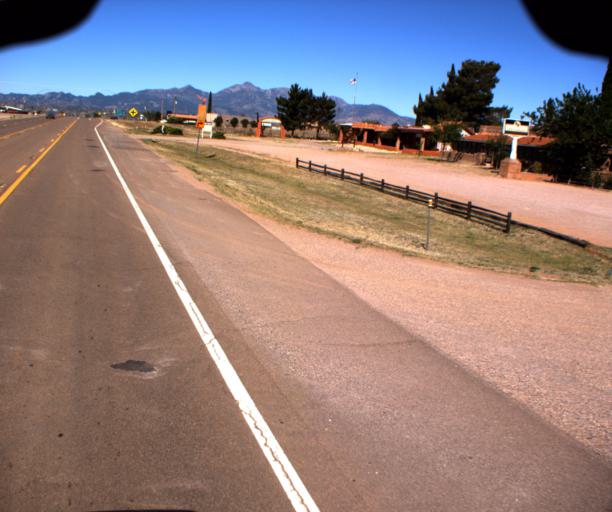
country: US
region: Arizona
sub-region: Pima County
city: Corona de Tucson
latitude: 31.6797
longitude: -110.6531
